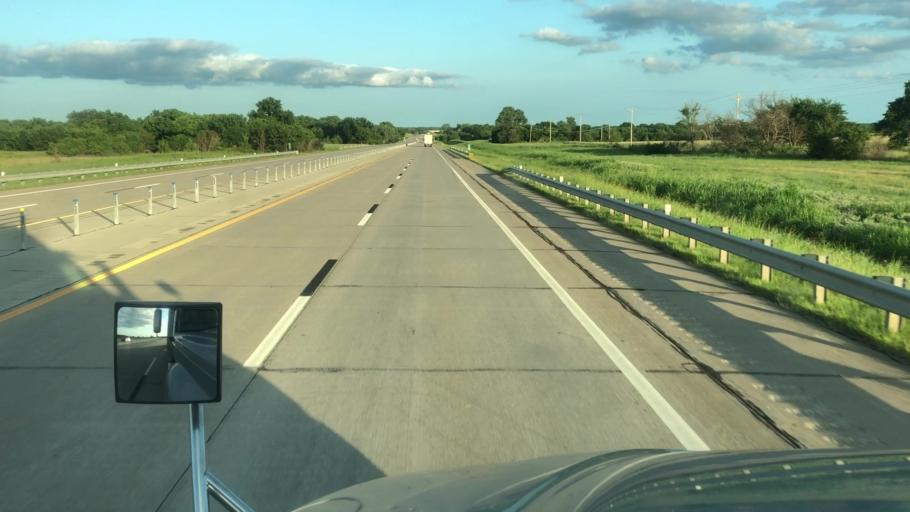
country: US
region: Oklahoma
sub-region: Pawnee County
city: Pawnee
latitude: 36.3293
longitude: -97.0098
